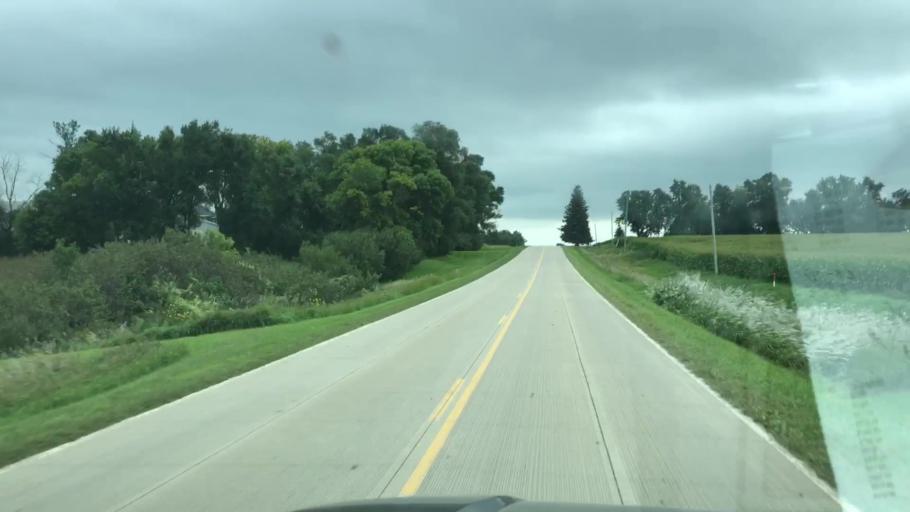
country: US
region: Iowa
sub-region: Sioux County
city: Alton
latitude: 43.1112
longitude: -95.9787
